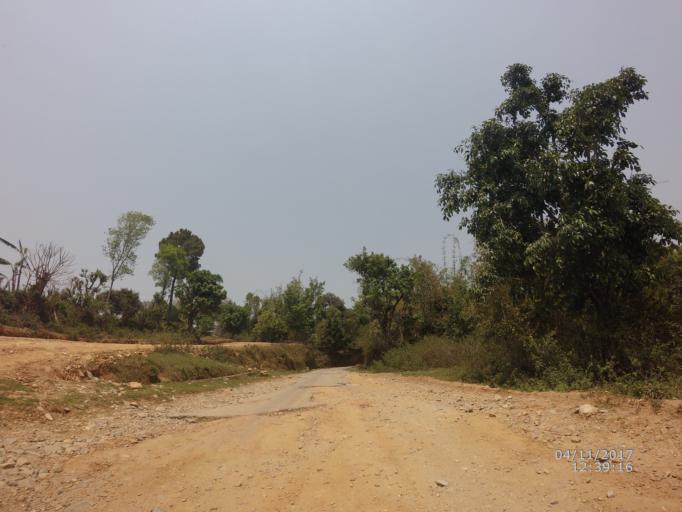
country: NP
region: Western Region
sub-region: Gandaki Zone
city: Pokhara
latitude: 28.2025
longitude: 84.0296
